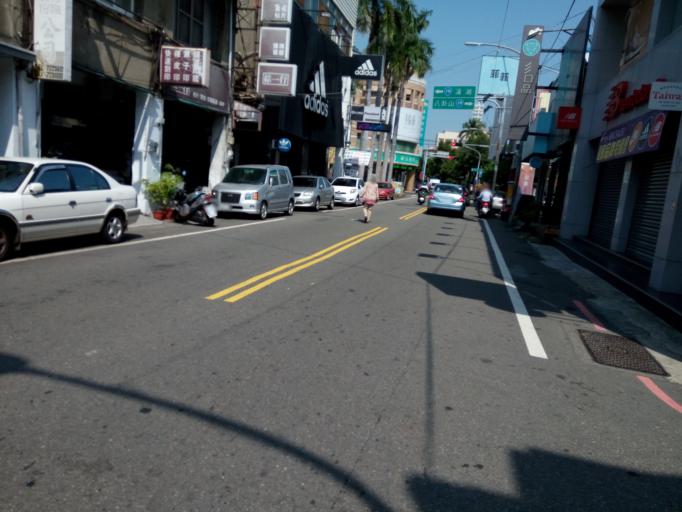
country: TW
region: Taiwan
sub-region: Changhua
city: Chang-hua
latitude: 24.0777
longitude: 120.5429
